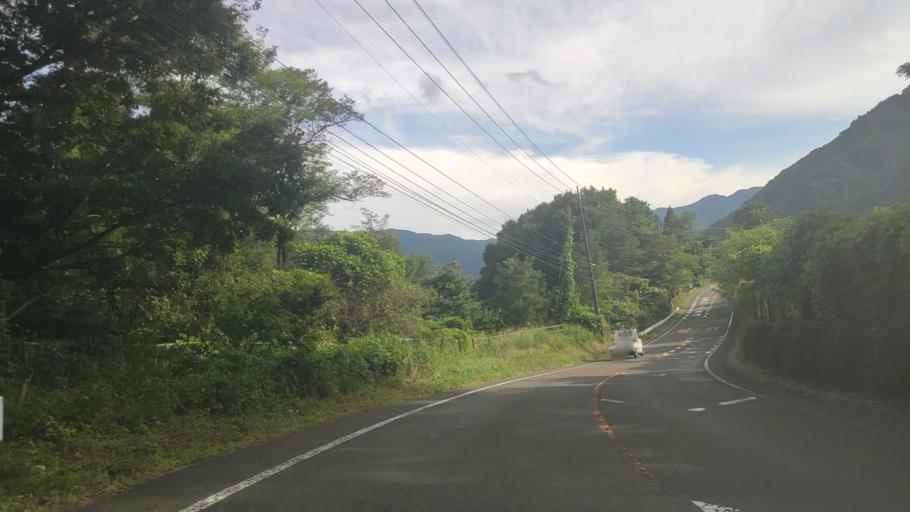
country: JP
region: Gunma
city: Omamacho-omama
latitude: 36.5575
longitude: 139.3759
